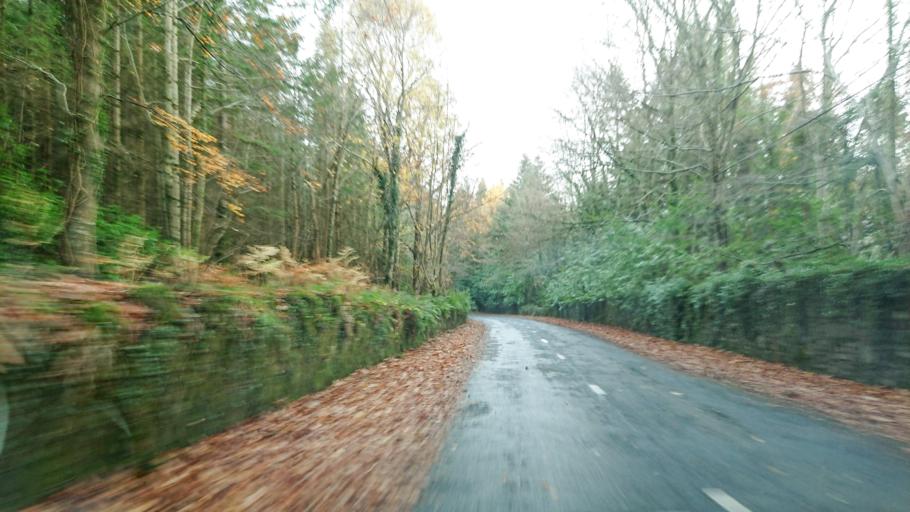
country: IE
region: Munster
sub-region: South Tipperary
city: Cluain Meala
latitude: 52.3567
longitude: -7.5906
